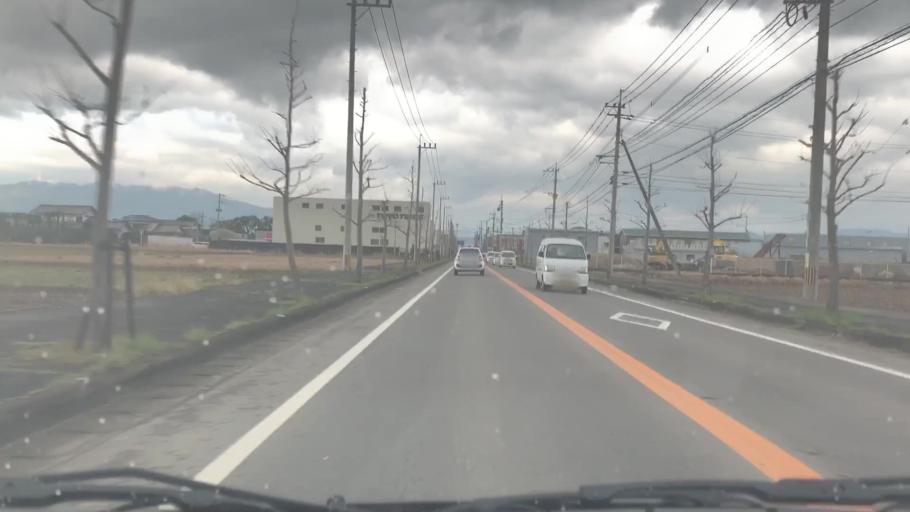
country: JP
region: Saga Prefecture
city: Saga-shi
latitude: 33.2515
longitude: 130.2648
